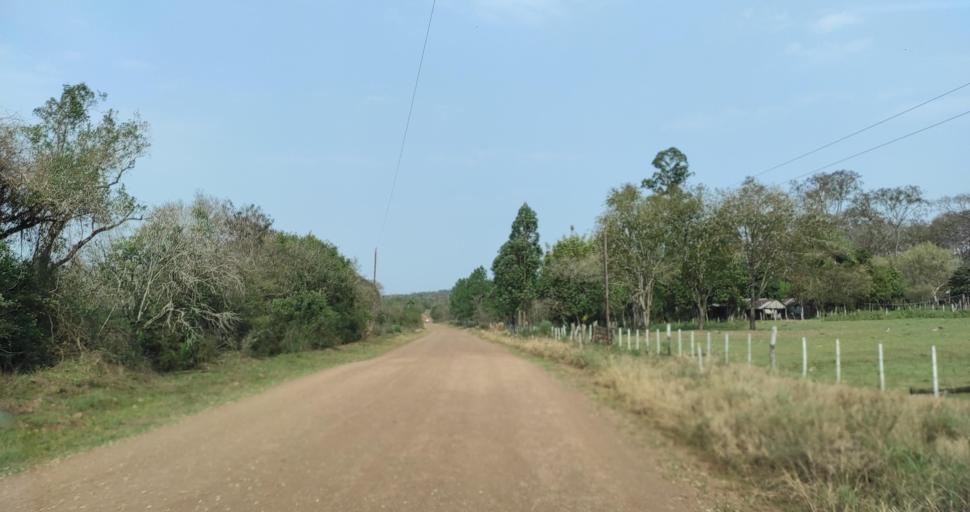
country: AR
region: Misiones
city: Cerro Cora
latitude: -27.5167
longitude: -55.6028
